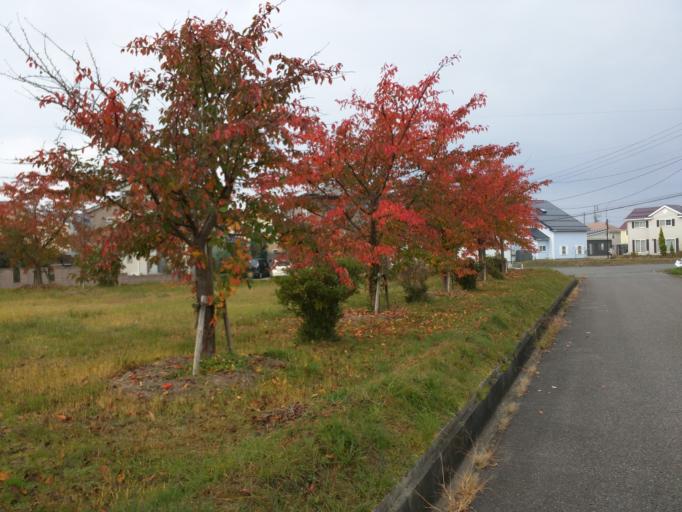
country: JP
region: Fukushima
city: Kitakata
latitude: 37.5291
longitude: 139.9630
